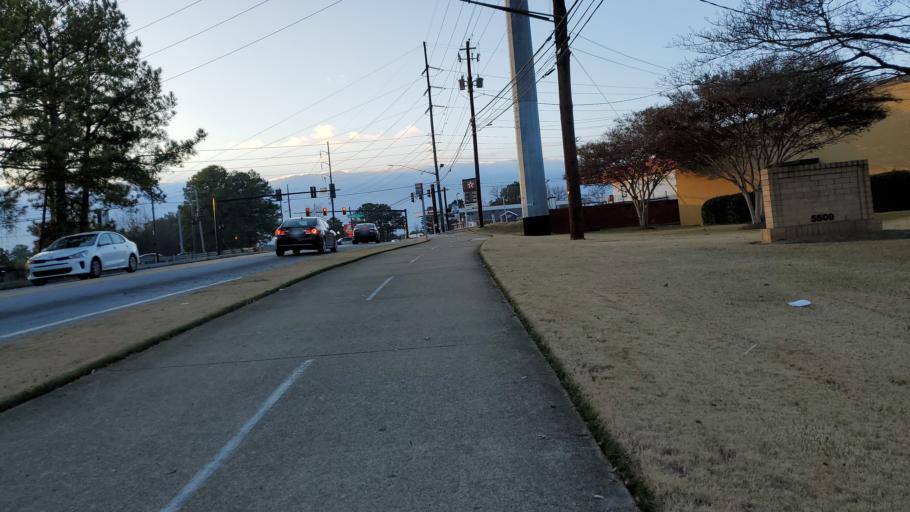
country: US
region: Georgia
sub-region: DeKalb County
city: Stone Mountain
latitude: 33.8257
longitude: -84.1948
